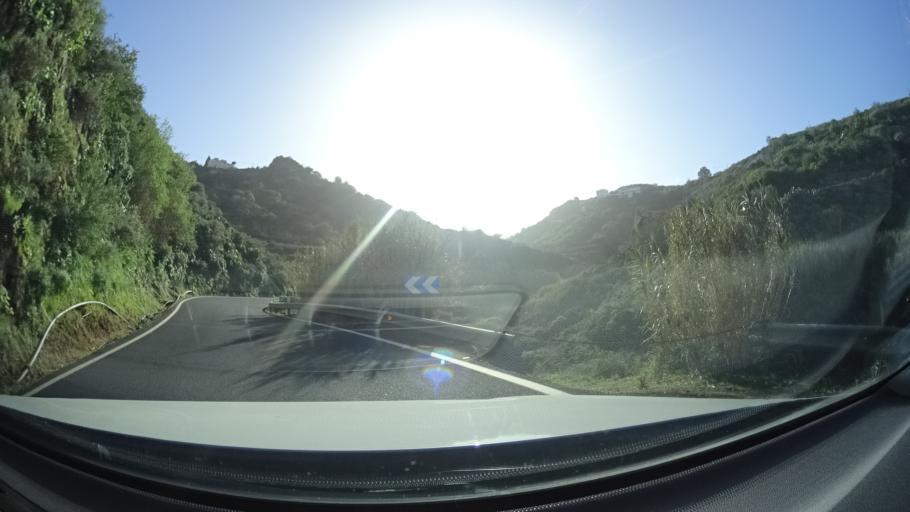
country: ES
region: Canary Islands
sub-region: Provincia de Las Palmas
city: Vega de San Mateo
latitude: 28.0257
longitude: -15.5547
